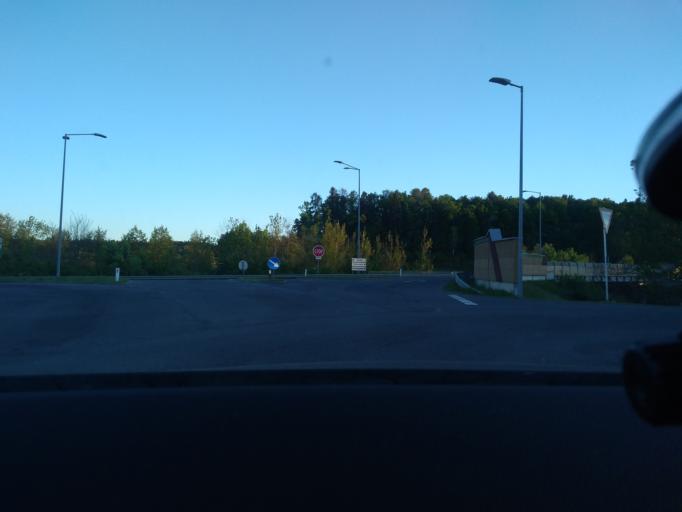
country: AT
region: Styria
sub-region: Politischer Bezirk Deutschlandsberg
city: Lannach
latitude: 46.9470
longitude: 15.3293
